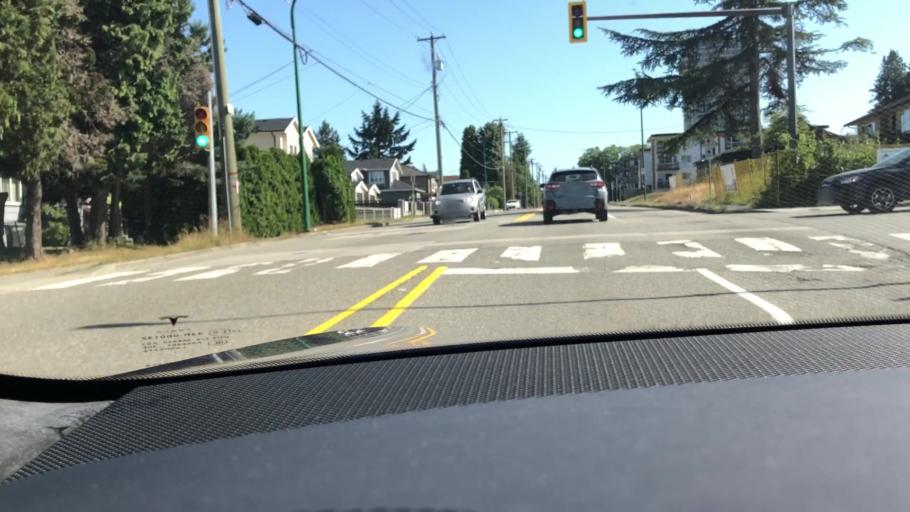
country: CA
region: British Columbia
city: Burnaby
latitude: 49.2280
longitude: -122.9890
